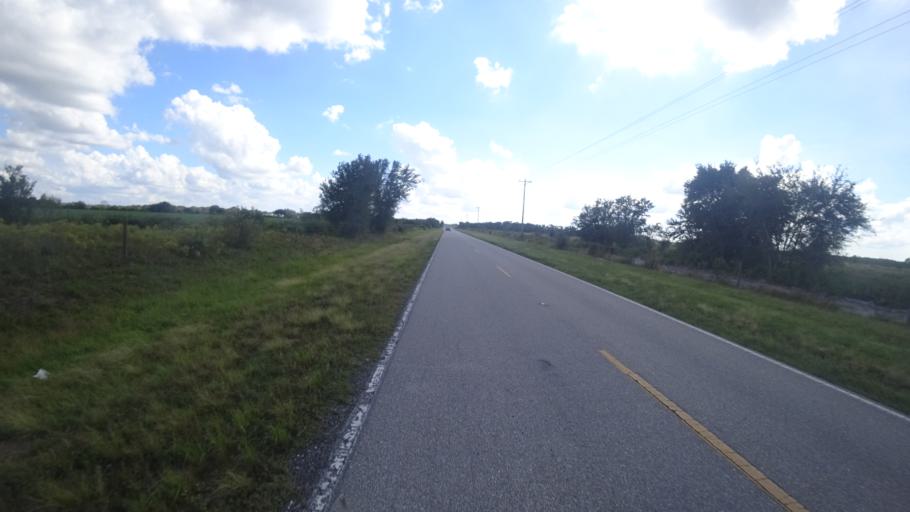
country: US
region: Florida
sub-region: Sarasota County
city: Lake Sarasota
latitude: 27.4203
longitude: -82.1332
